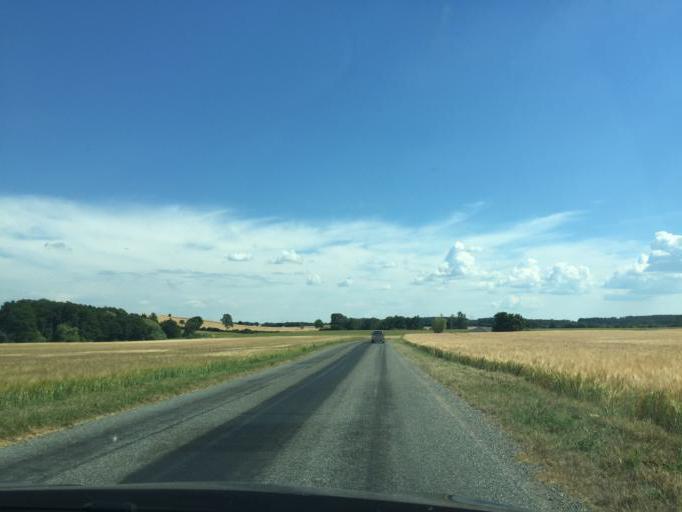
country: DK
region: South Denmark
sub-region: Odense Kommune
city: Bellinge
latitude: 55.2477
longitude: 10.2843
